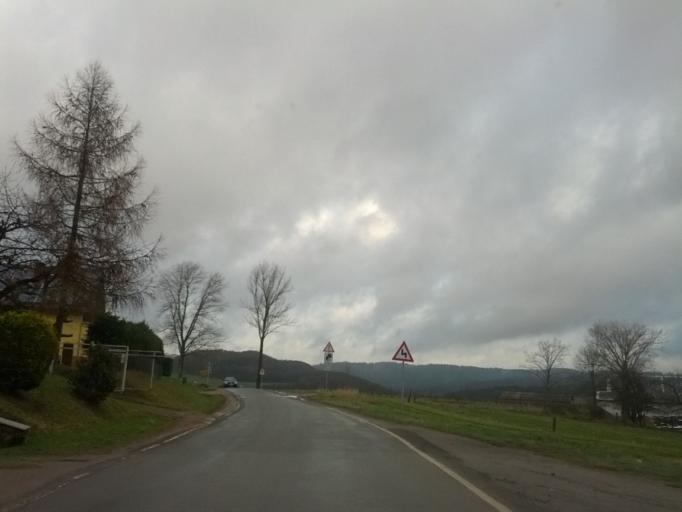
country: DE
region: Thuringia
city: Wolfsburg-Unkeroda
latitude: 50.9178
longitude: 10.2648
